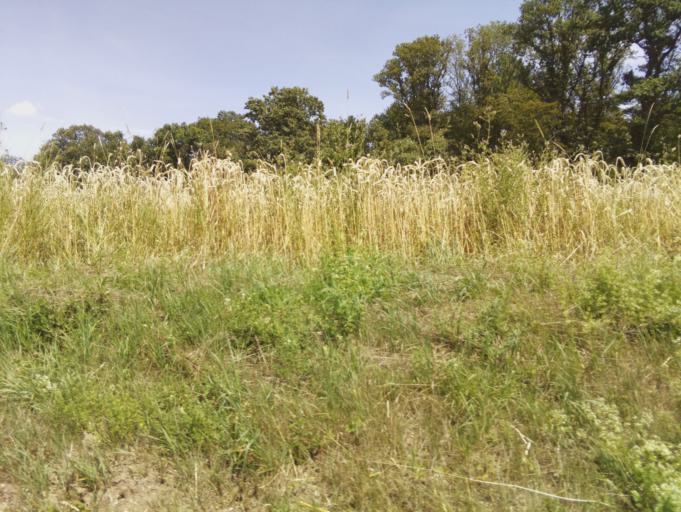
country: CH
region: Zurich
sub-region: Bezirk Andelfingen
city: Marthalen
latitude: 47.6321
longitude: 8.6614
